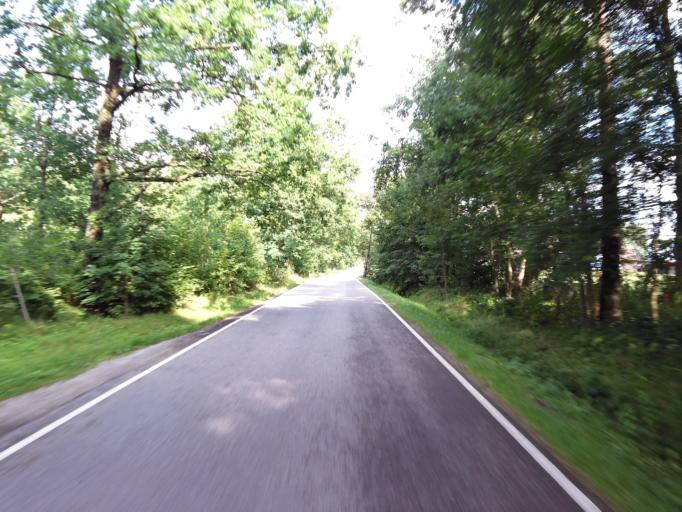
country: CZ
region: Jihocesky
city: Suchdol nad Luznici
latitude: 48.8886
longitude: 14.8375
